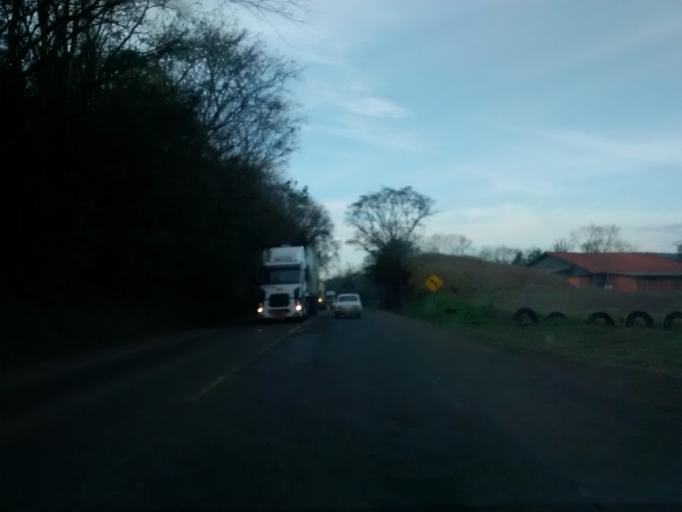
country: BR
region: Parana
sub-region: Francisco Beltrao
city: Francisco Beltrao
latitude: -26.1050
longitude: -53.0577
